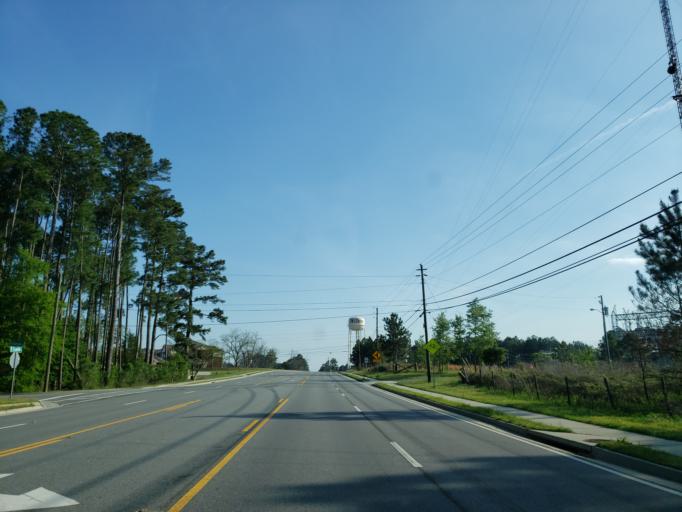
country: US
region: Georgia
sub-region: Tift County
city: Tifton
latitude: 31.4765
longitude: -83.5429
